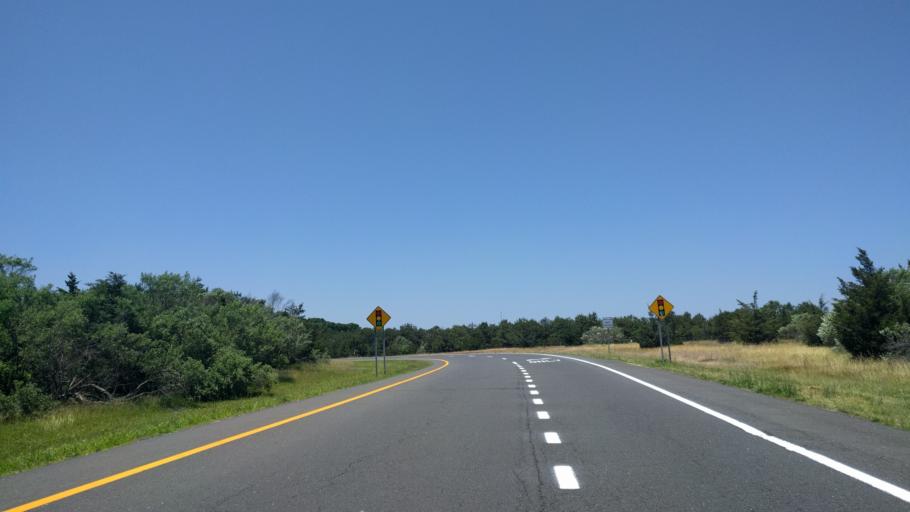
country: US
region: New York
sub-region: Suffolk County
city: Eastport
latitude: 40.8462
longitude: -72.7232
